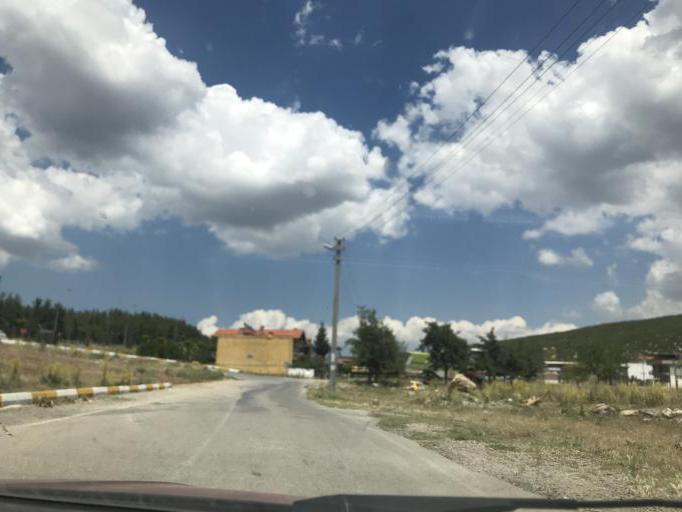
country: TR
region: Denizli
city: Tavas
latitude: 37.5718
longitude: 29.0803
